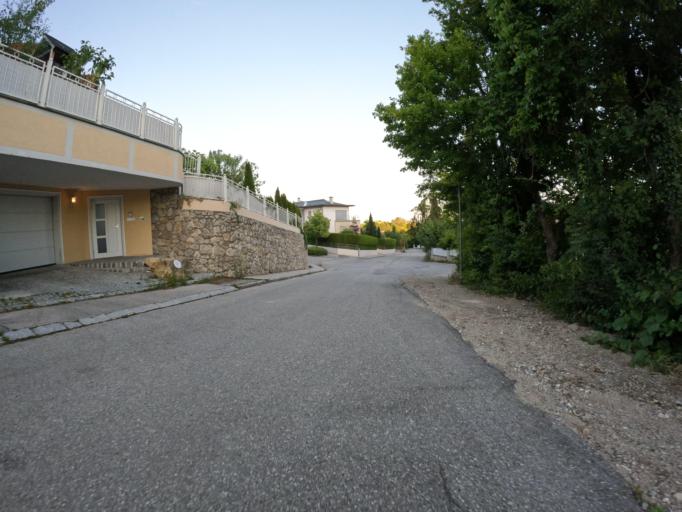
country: AT
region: Lower Austria
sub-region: Politischer Bezirk Baden
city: Baden
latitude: 48.0142
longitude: 16.2202
